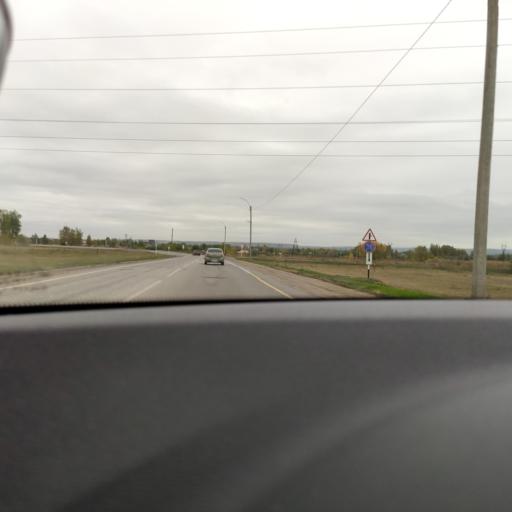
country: RU
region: Samara
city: Krasnyy Yar
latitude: 53.4762
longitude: 50.3914
